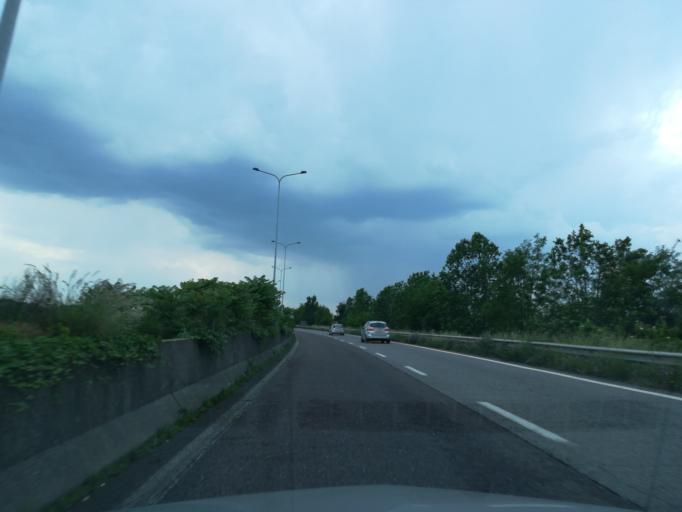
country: IT
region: Lombardy
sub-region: Provincia di Bergamo
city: Orio al Serio
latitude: 45.6796
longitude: 9.6921
